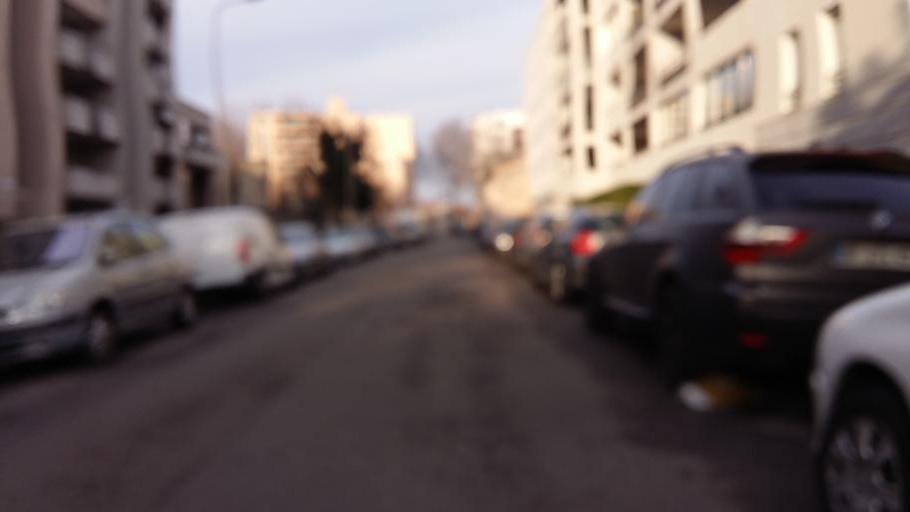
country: FR
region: Rhone-Alpes
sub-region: Departement du Rhone
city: Lyon
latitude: 45.7380
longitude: 4.8280
